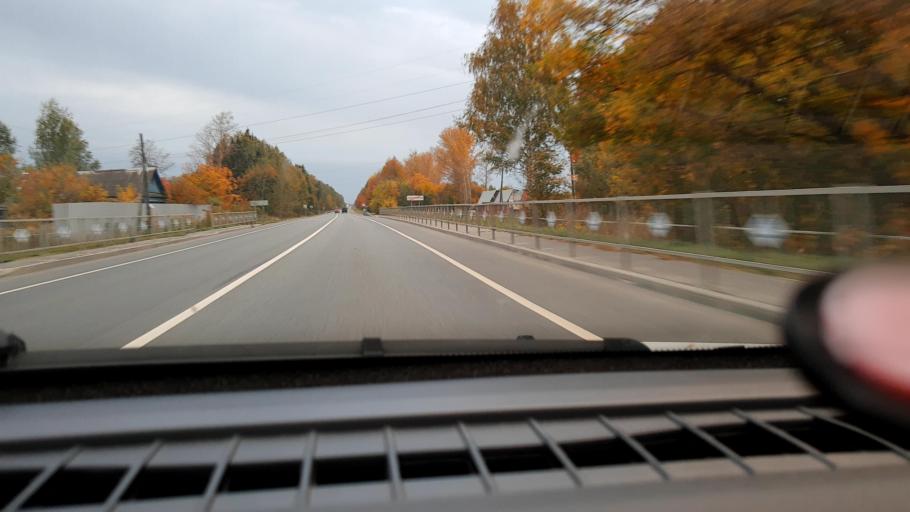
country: RU
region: Vladimir
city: Orgtrud
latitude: 56.1988
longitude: 40.8373
